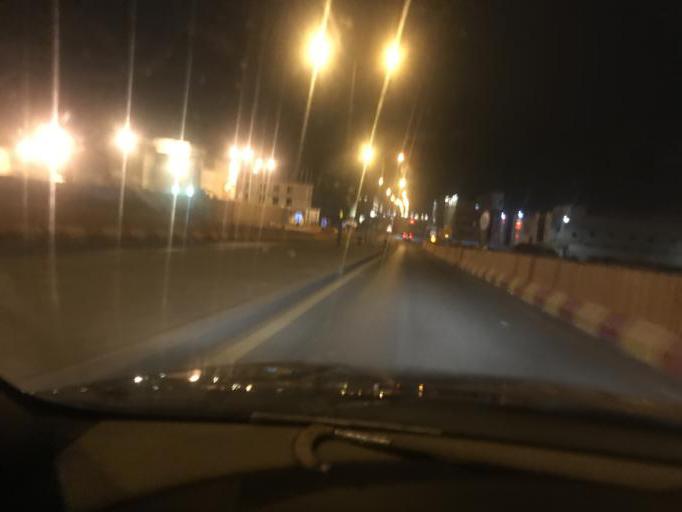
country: SA
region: Ar Riyad
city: Riyadh
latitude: 24.8002
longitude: 46.6846
